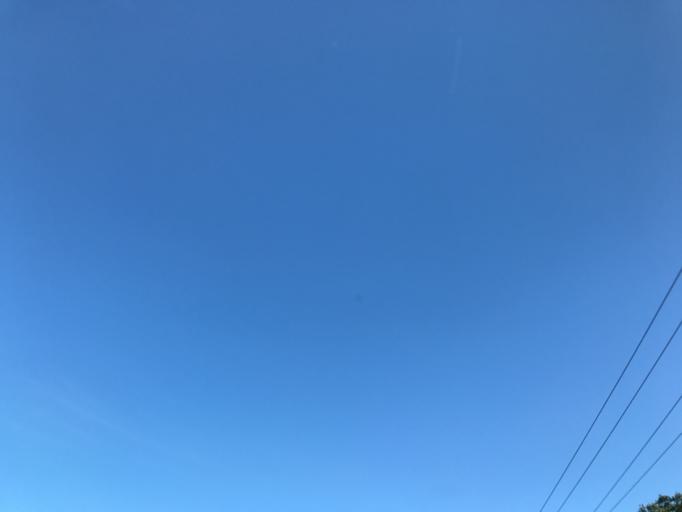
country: US
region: Massachusetts
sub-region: Essex County
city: Saugus
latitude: 42.5017
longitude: -71.0145
